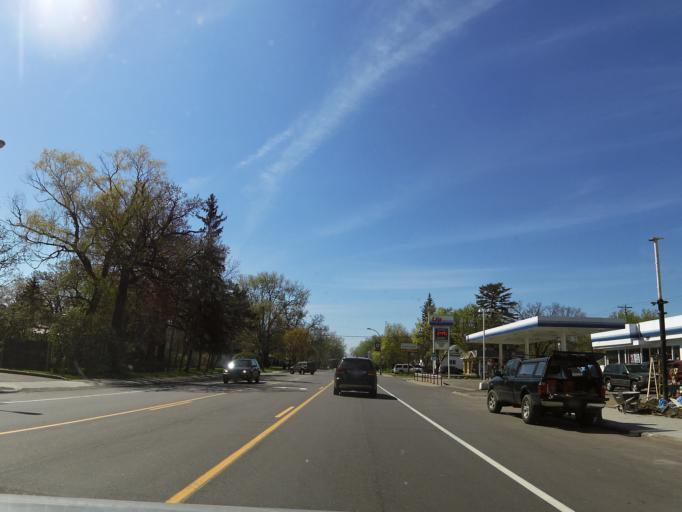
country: US
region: Minnesota
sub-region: Hennepin County
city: Richfield
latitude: 44.8806
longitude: -93.3087
